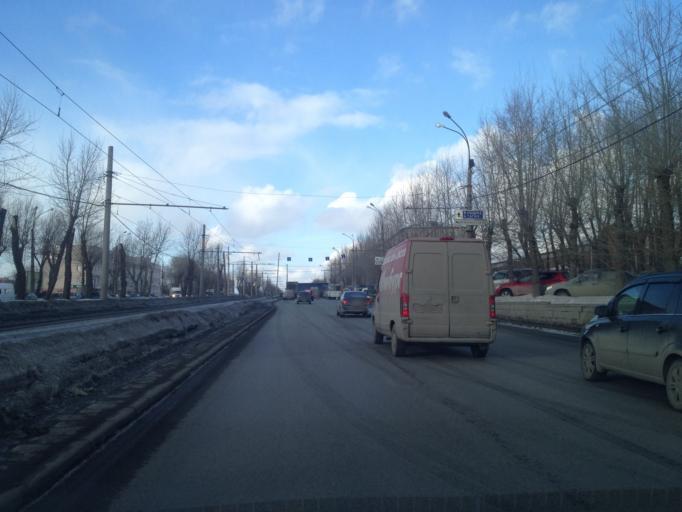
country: RU
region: Sverdlovsk
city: Yekaterinburg
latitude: 56.8692
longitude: 60.6118
